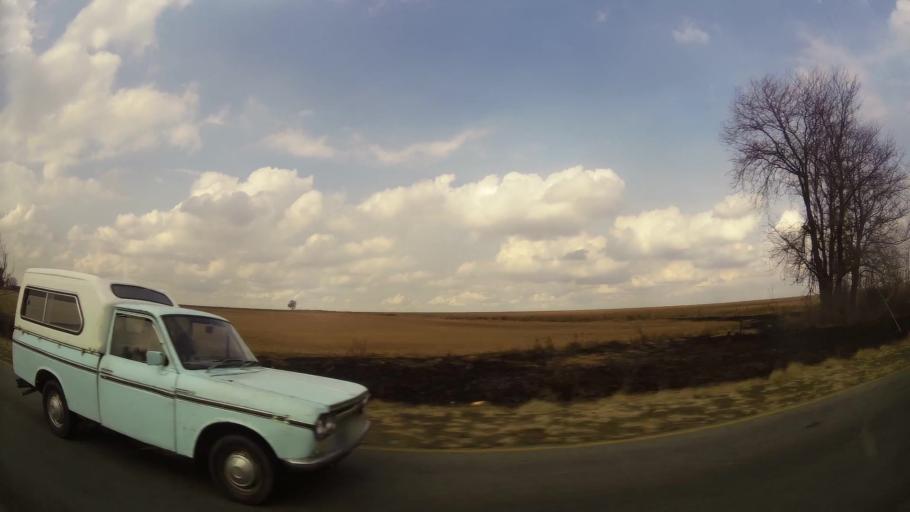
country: ZA
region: Orange Free State
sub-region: Fezile Dabi District Municipality
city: Sasolburg
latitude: -26.8329
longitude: 27.8975
